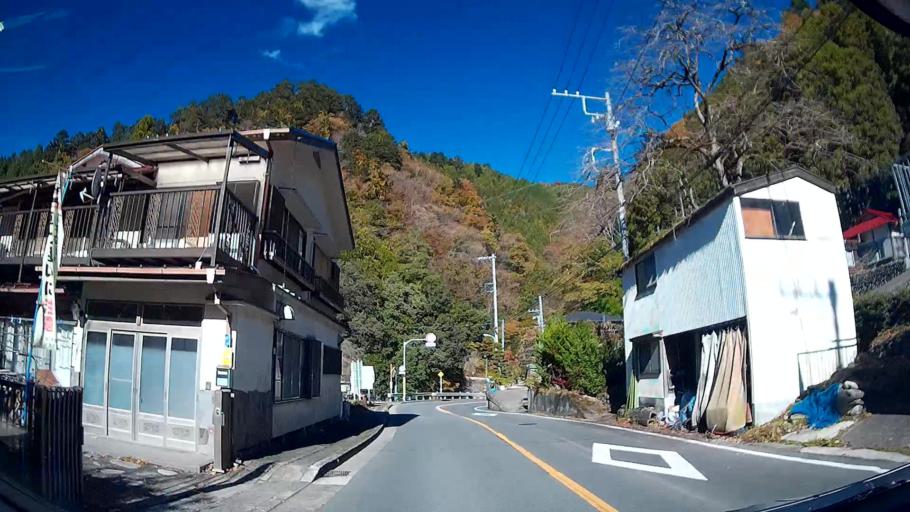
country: JP
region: Yamanashi
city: Uenohara
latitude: 35.7034
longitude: 139.1316
